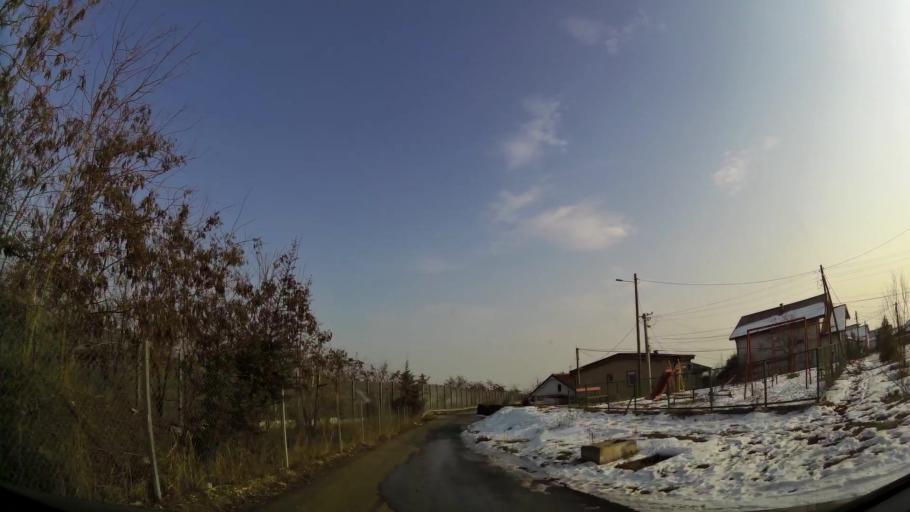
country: MK
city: Creshevo
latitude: 42.0320
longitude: 21.5262
